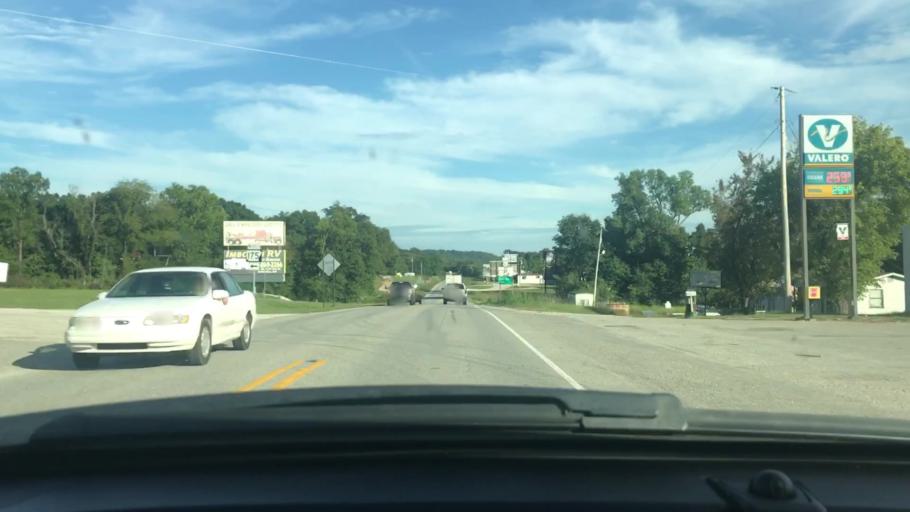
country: US
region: Arkansas
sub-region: Sharp County
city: Cherokee Village
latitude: 36.3024
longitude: -91.4450
